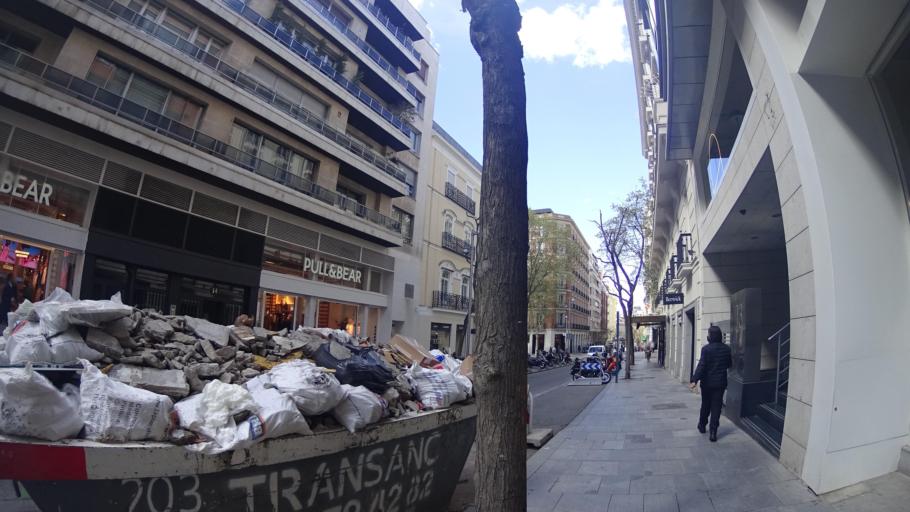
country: ES
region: Madrid
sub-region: Provincia de Madrid
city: Salamanca
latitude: 40.4265
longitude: -3.6870
